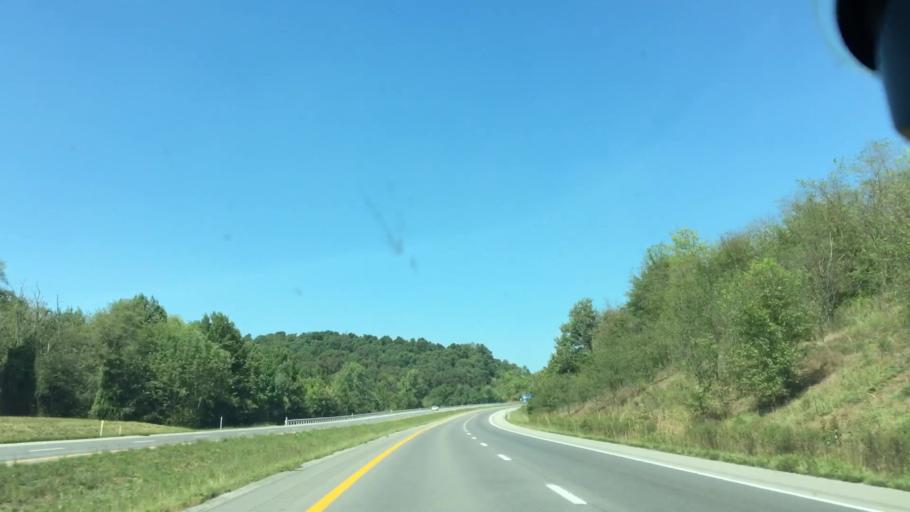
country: US
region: Kentucky
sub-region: Webster County
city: Sebree
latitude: 37.5937
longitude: -87.4939
